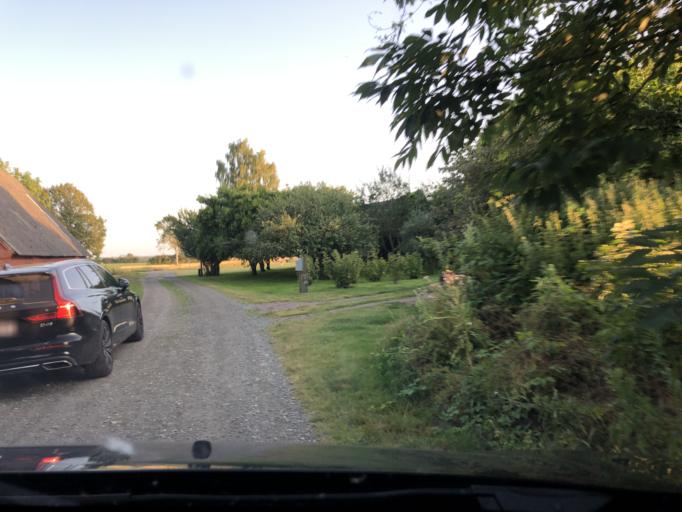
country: DK
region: South Denmark
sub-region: Vejle Kommune
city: Brejning
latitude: 55.6490
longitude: 9.7190
